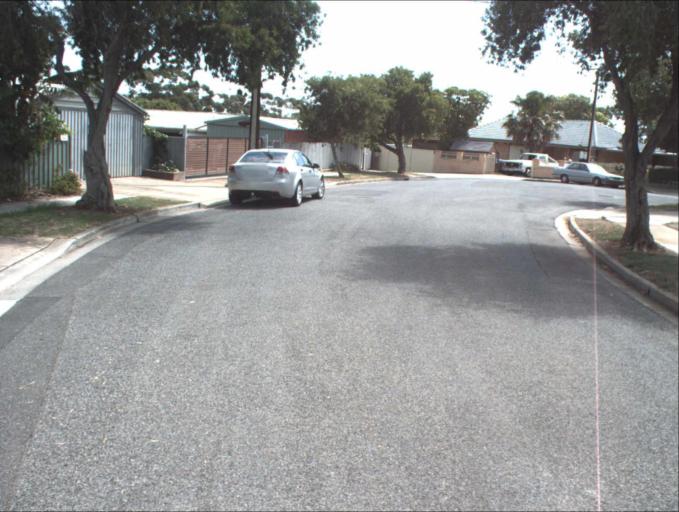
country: AU
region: South Australia
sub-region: Salisbury
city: Ingle Farm
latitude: -34.8419
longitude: 138.6222
